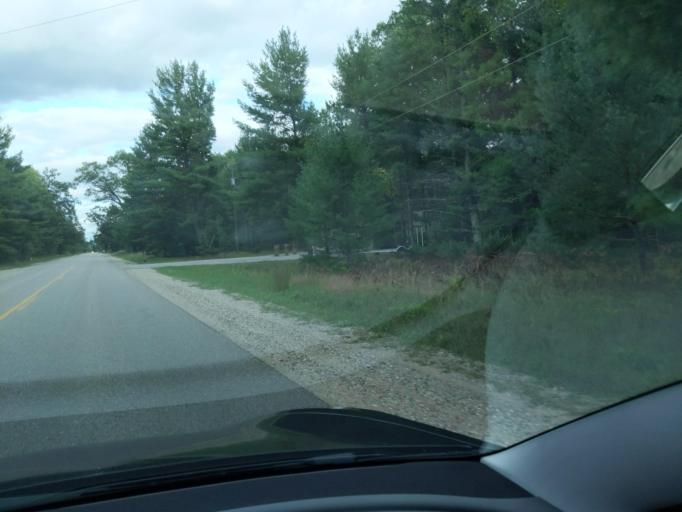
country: US
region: Michigan
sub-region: Kalkaska County
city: Rapid City
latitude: 44.8427
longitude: -85.3040
